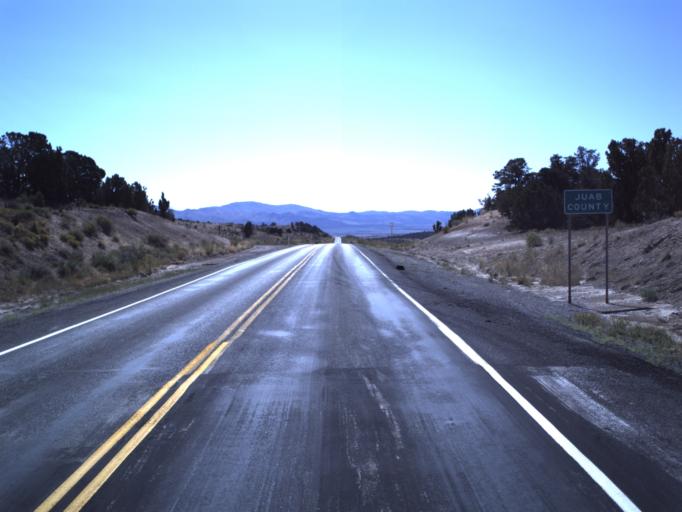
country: US
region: Utah
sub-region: Utah County
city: Genola
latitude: 39.9572
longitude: -112.2433
